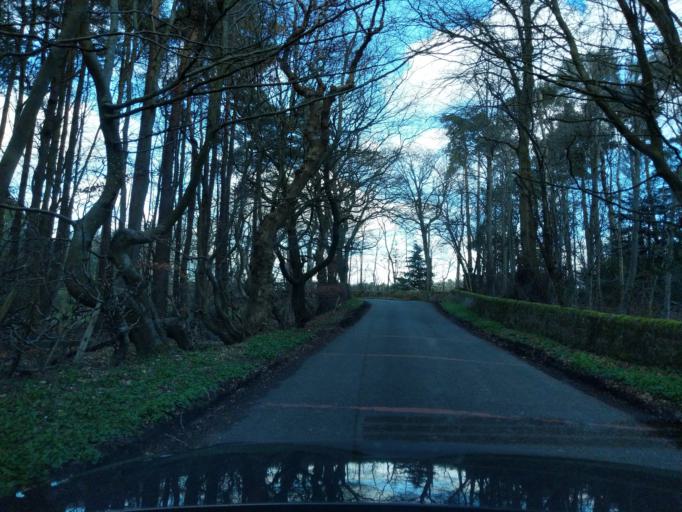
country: GB
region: Scotland
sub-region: Edinburgh
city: Balerno
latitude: 55.8772
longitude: -3.3697
